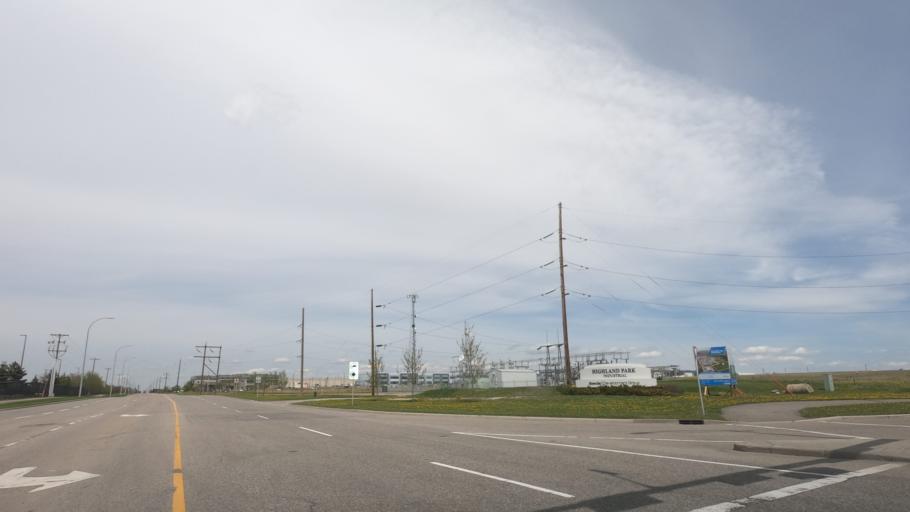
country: CA
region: Alberta
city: Airdrie
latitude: 51.3001
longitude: -113.9899
